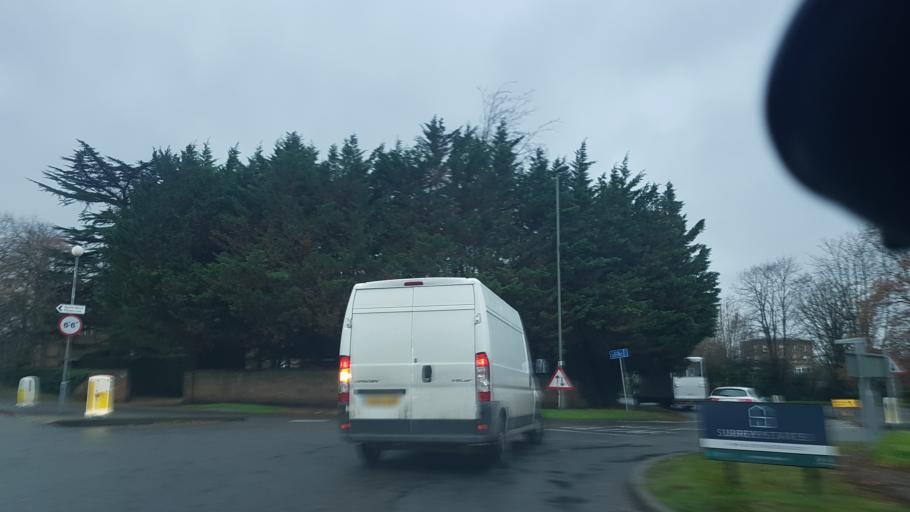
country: GB
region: England
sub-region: Surrey
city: Chilworth
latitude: 51.2471
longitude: -0.5255
